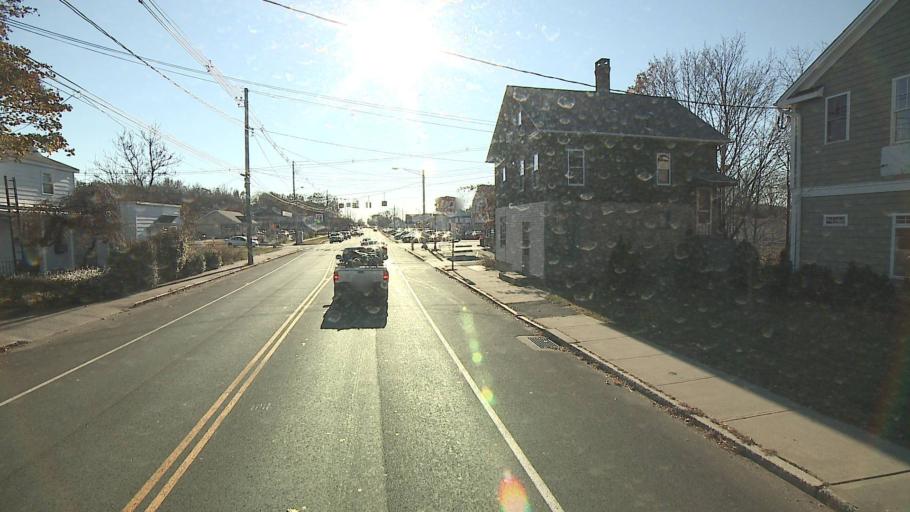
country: US
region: Connecticut
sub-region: New Haven County
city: Wallingford
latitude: 41.4529
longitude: -72.8263
